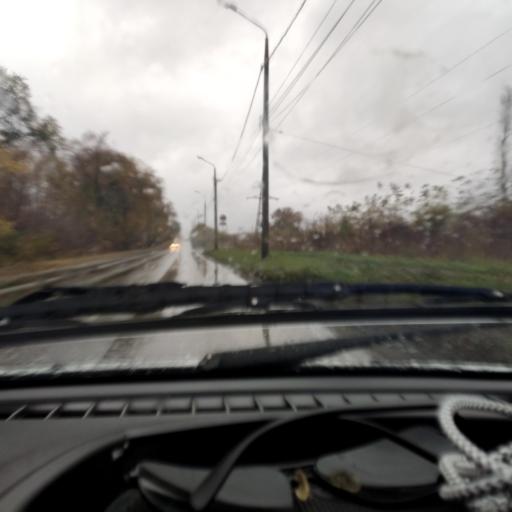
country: RU
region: Samara
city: Zhigulevsk
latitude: 53.4633
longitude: 49.5648
